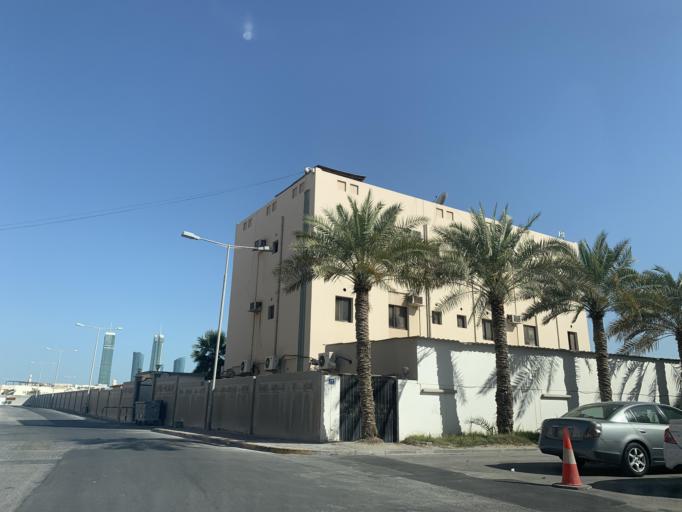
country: BH
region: Manama
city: Manama
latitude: 26.2217
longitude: 50.5801
